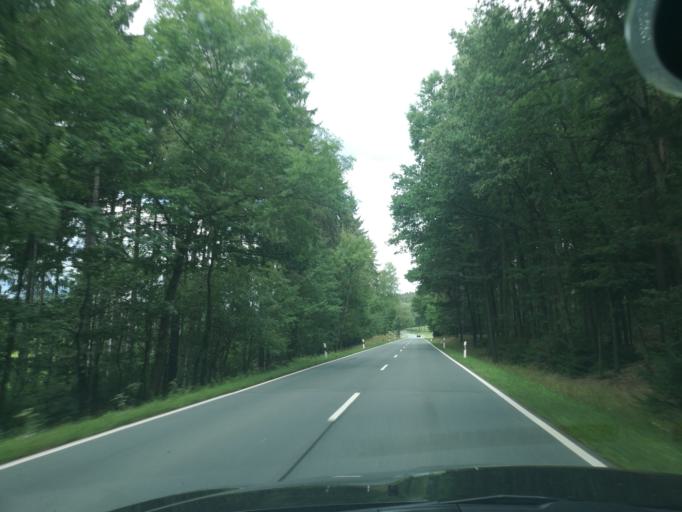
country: DE
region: Saxony
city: Eichigt
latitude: 50.3774
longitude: 12.2047
